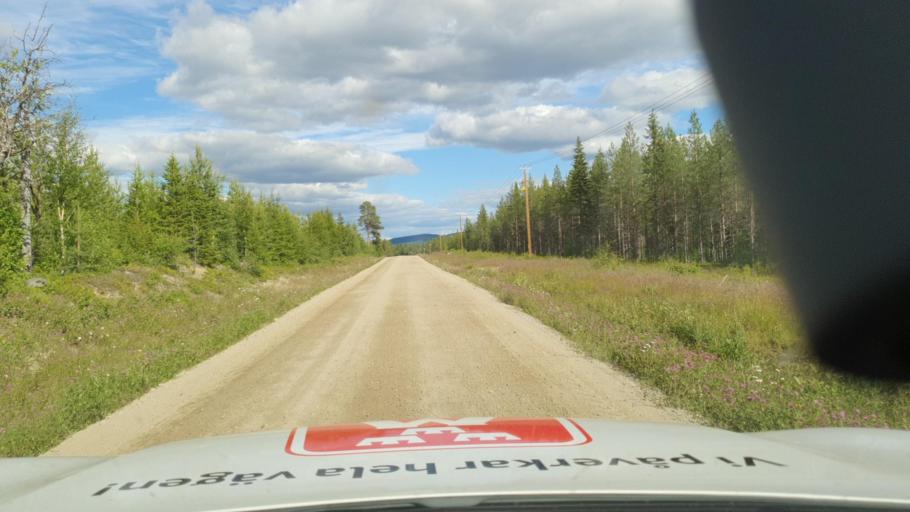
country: SE
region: Vaesterbotten
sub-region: Lycksele Kommun
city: Lycksele
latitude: 64.2949
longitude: 18.2552
